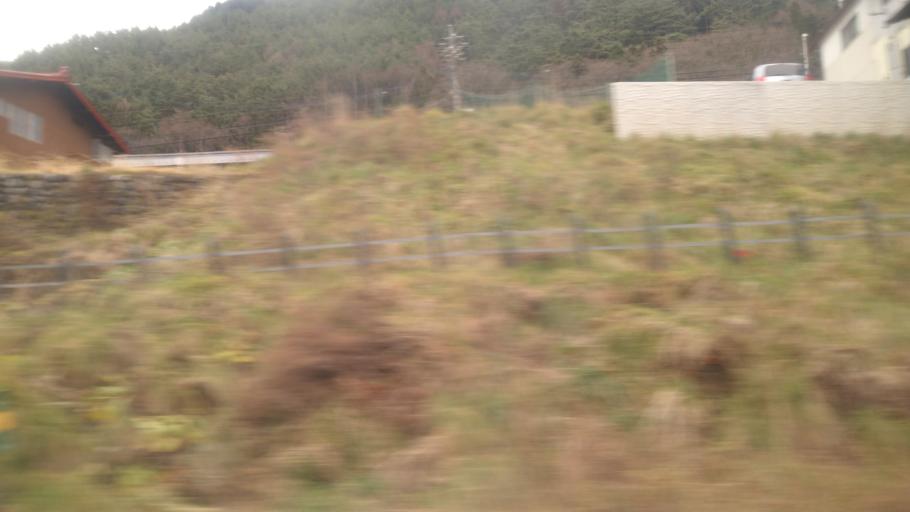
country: JP
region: Nagano
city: Shiojiri
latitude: 36.0590
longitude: 137.9009
